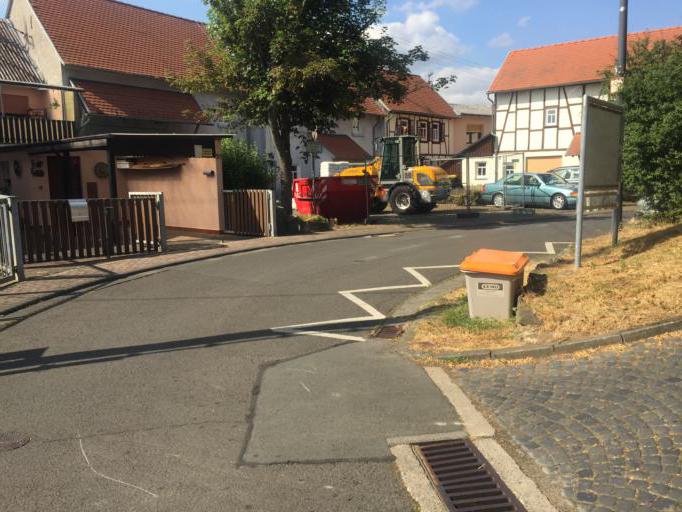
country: DE
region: Hesse
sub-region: Regierungsbezirk Giessen
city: Heuchelheim
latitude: 50.6205
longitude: 8.6162
